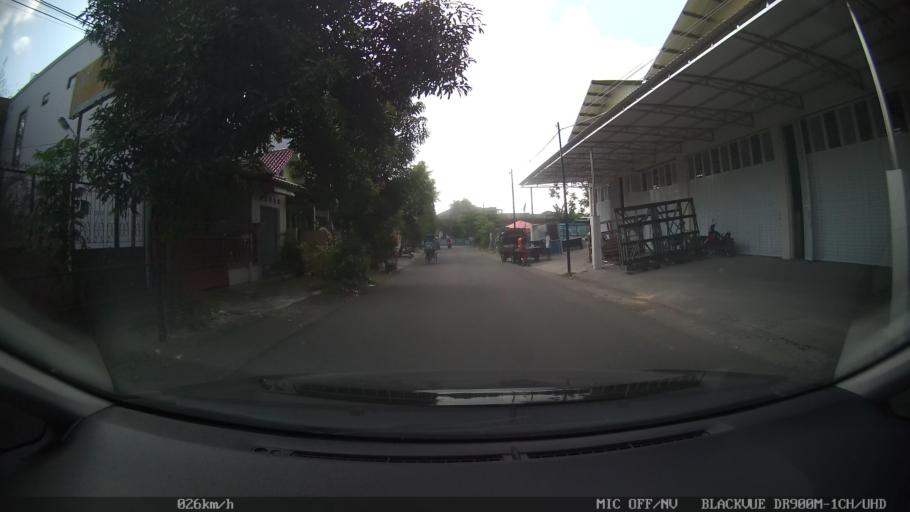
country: ID
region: Daerah Istimewa Yogyakarta
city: Kasihan
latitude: -7.8311
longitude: 110.3683
